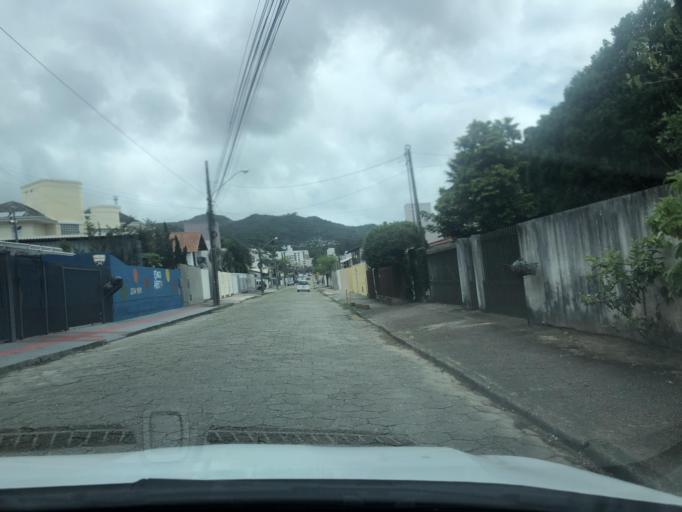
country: BR
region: Santa Catarina
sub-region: Florianopolis
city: Santa Monica
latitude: -27.5947
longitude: -48.5123
